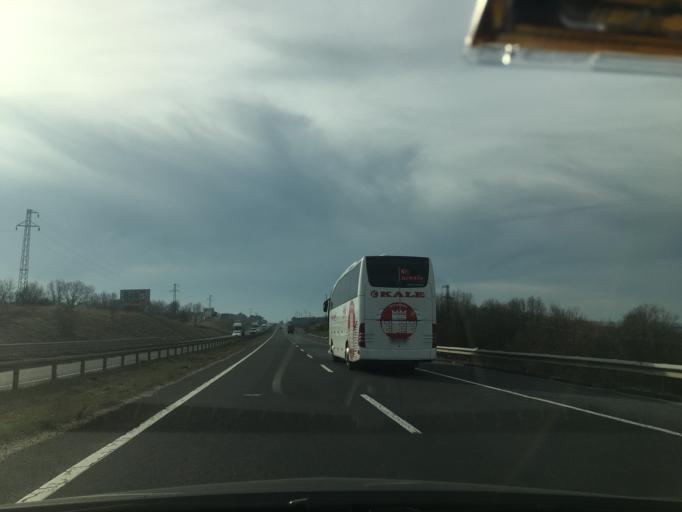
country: TR
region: Istanbul
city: Buyukcavuslu
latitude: 41.2127
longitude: 28.0718
